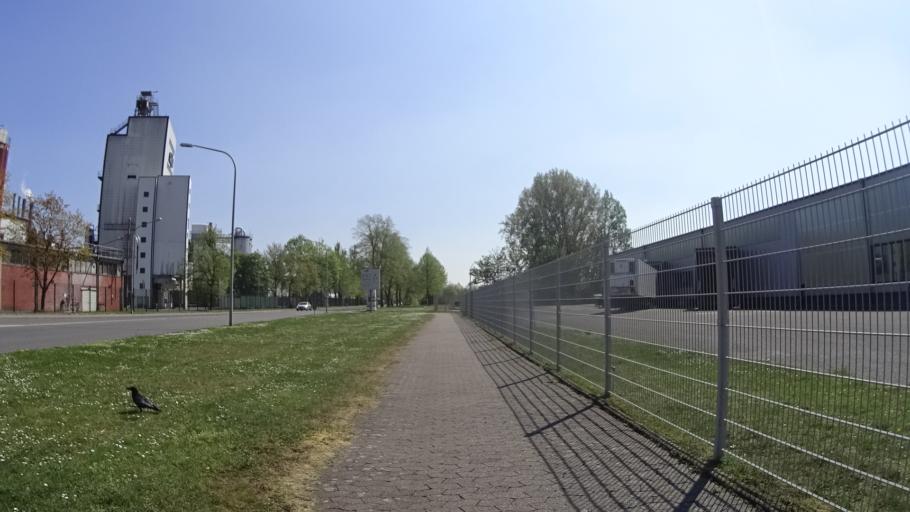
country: DE
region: North Rhine-Westphalia
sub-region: Regierungsbezirk Dusseldorf
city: Krefeld
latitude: 51.3409
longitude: 6.6604
